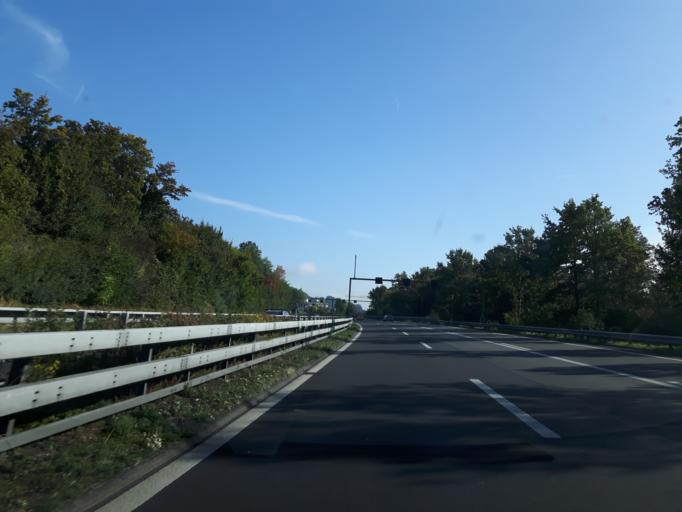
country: CH
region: Lucerne
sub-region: Sursee District
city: Eich
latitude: 47.1547
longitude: 8.1595
